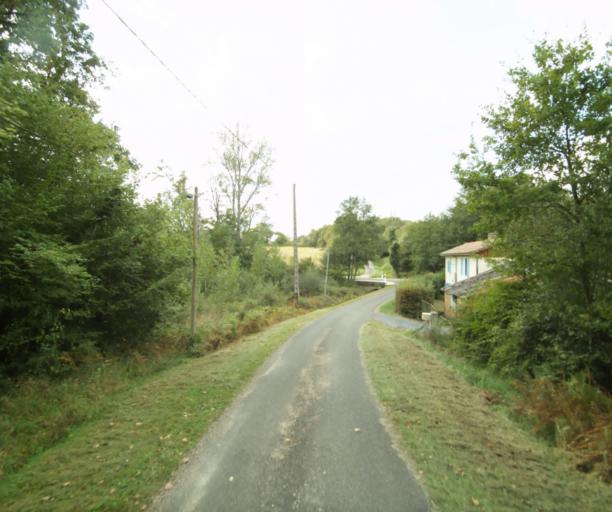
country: FR
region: Midi-Pyrenees
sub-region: Departement du Gers
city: Cazaubon
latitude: 43.8943
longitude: -0.0918
